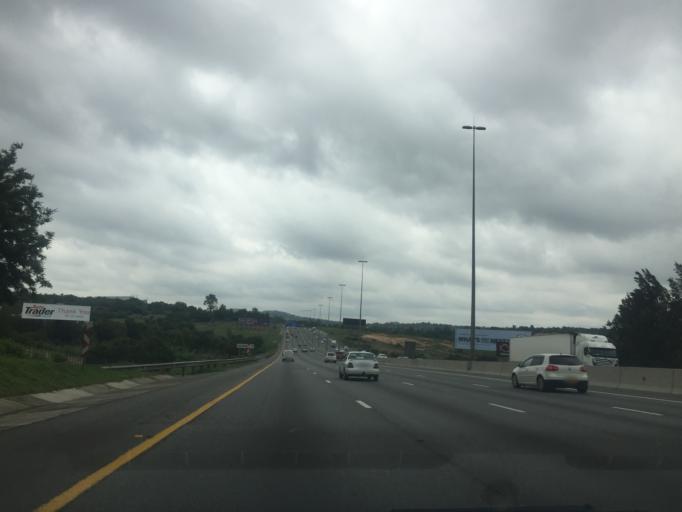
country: ZA
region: Gauteng
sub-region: City of Johannesburg Metropolitan Municipality
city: Diepsloot
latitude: -26.0610
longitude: 27.9843
